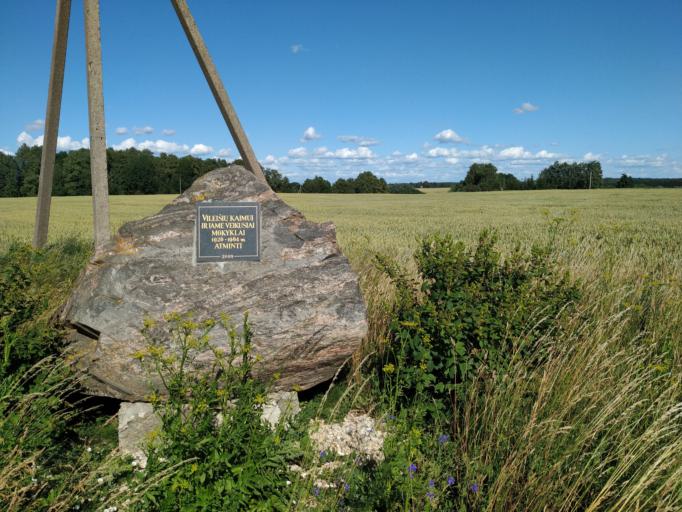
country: LT
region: Panevezys
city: Pasvalys
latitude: 56.1688
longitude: 24.4266
